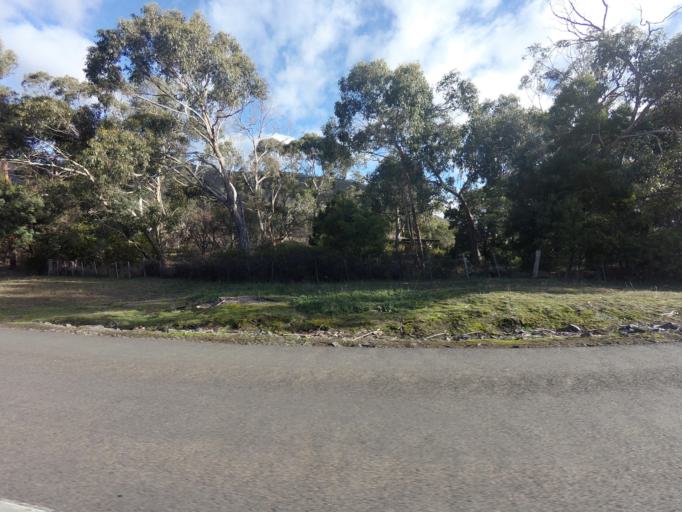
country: AU
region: Tasmania
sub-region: Derwent Valley
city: New Norfolk
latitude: -42.7916
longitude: 147.1230
